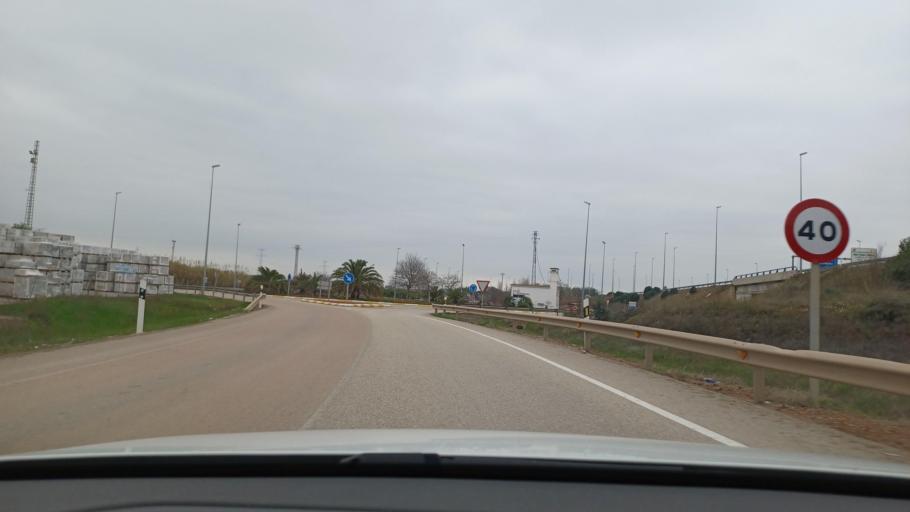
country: ES
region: Valencia
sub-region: Provincia de Castello
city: Villavieja
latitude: 39.8563
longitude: -0.1711
